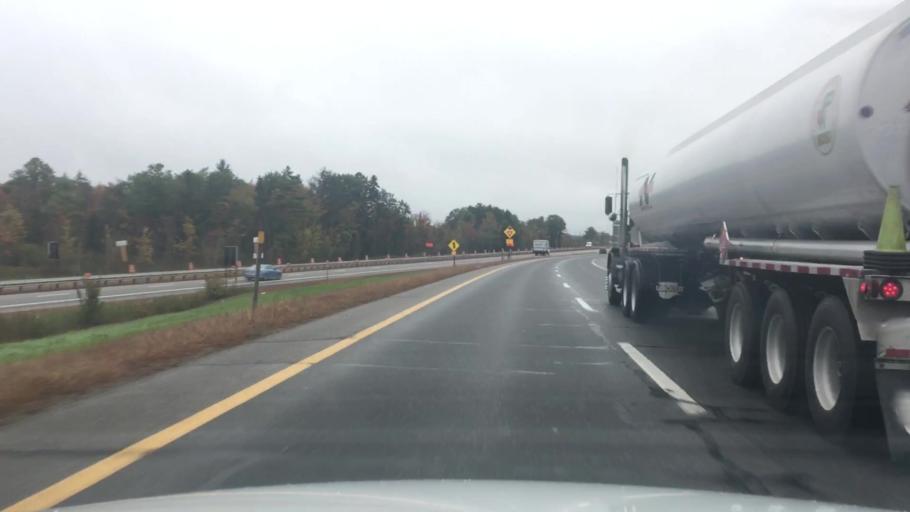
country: US
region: Maine
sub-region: Kennebec County
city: Gardiner
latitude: 44.2187
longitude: -69.8224
